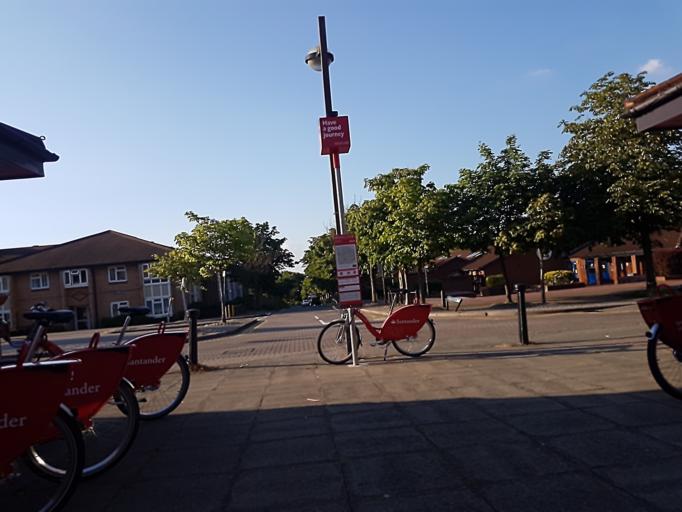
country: GB
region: England
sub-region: Milton Keynes
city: Loughton
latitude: 52.0379
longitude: -0.8017
